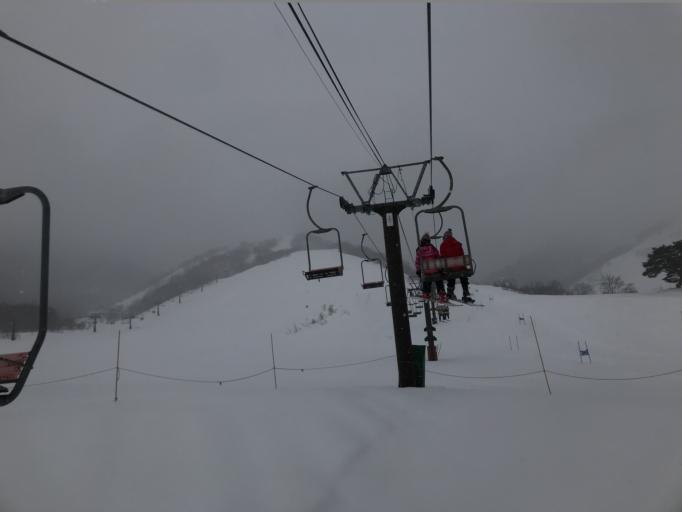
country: JP
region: Nagano
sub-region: Kitaazumi Gun
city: Hakuba
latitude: 36.7575
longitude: 137.8638
